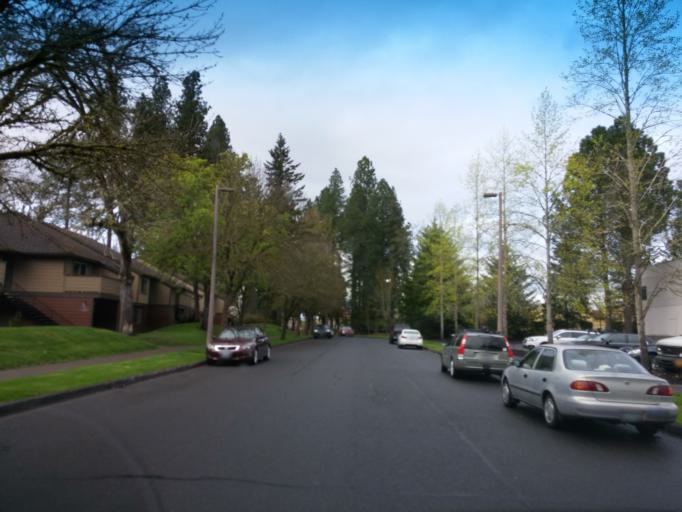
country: US
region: Oregon
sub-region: Washington County
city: Oak Hills
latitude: 45.5149
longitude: -122.8420
